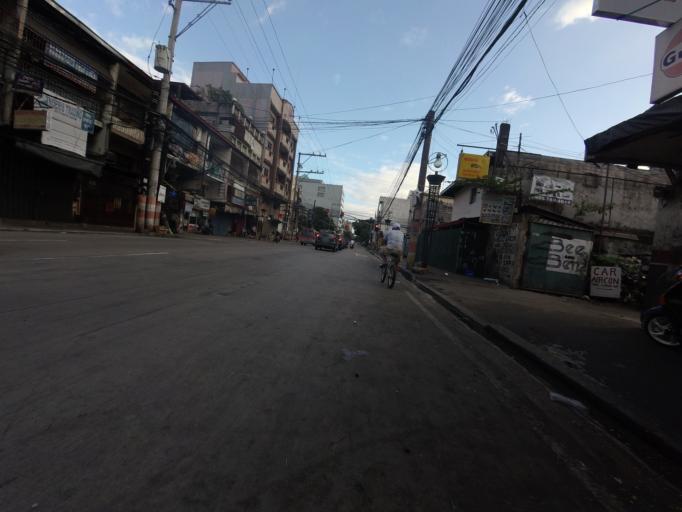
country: PH
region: Metro Manila
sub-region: City of Manila
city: Quiapo
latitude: 14.5774
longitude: 120.9902
